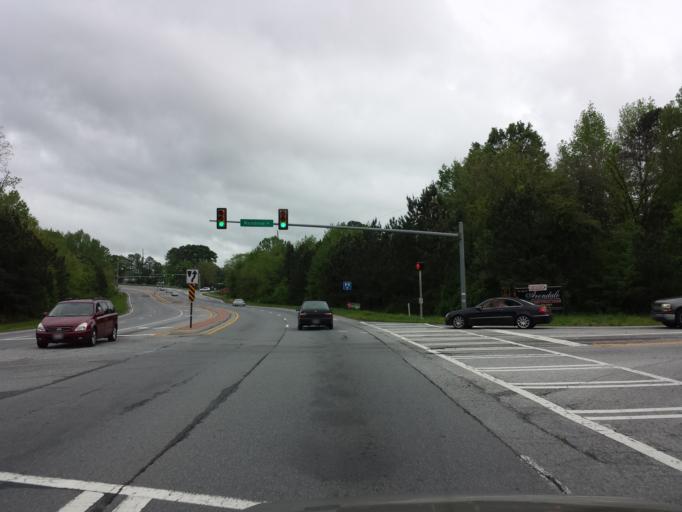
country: US
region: Georgia
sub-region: Cobb County
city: Powder Springs
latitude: 33.8715
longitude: -84.6347
